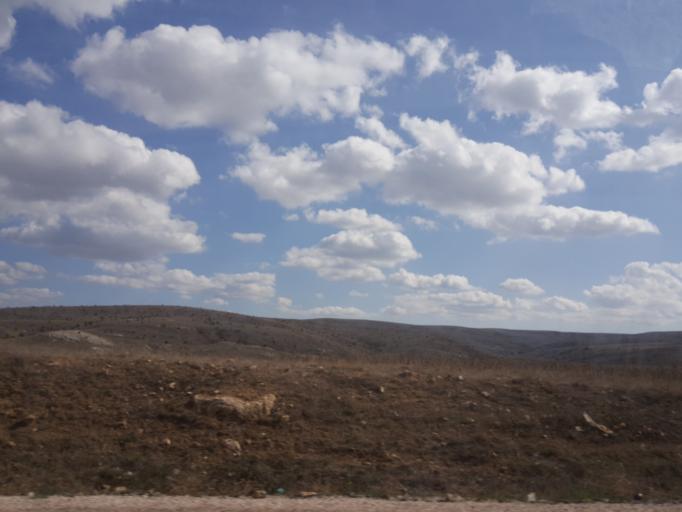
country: TR
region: Tokat
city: Camlibel
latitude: 40.1542
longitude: 36.3990
